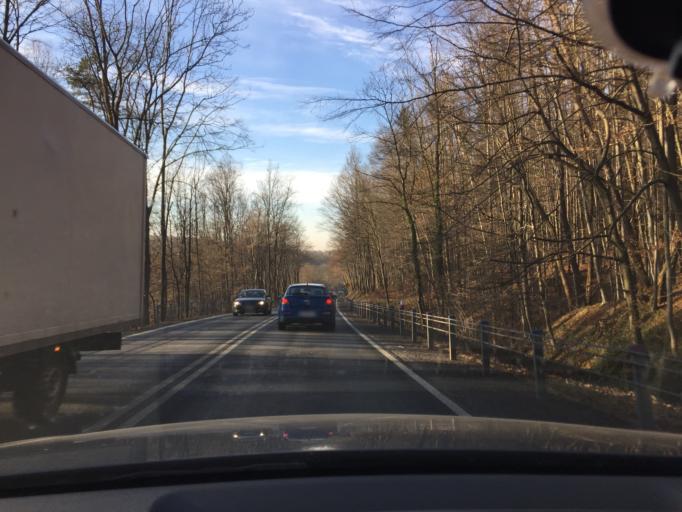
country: PL
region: Lesser Poland Voivodeship
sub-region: Powiat wadowicki
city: Lanckorona
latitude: 49.8650
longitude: 19.7307
